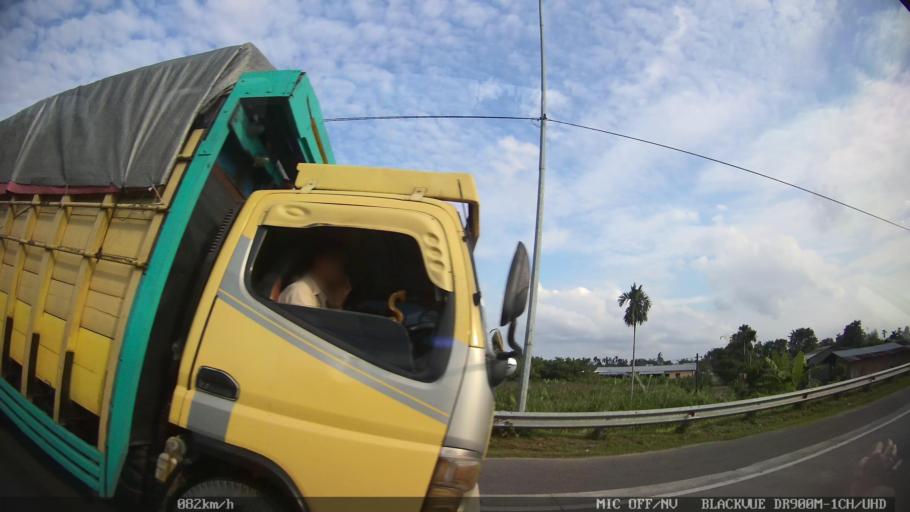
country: ID
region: North Sumatra
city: Medan
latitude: 3.6477
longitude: 98.6527
